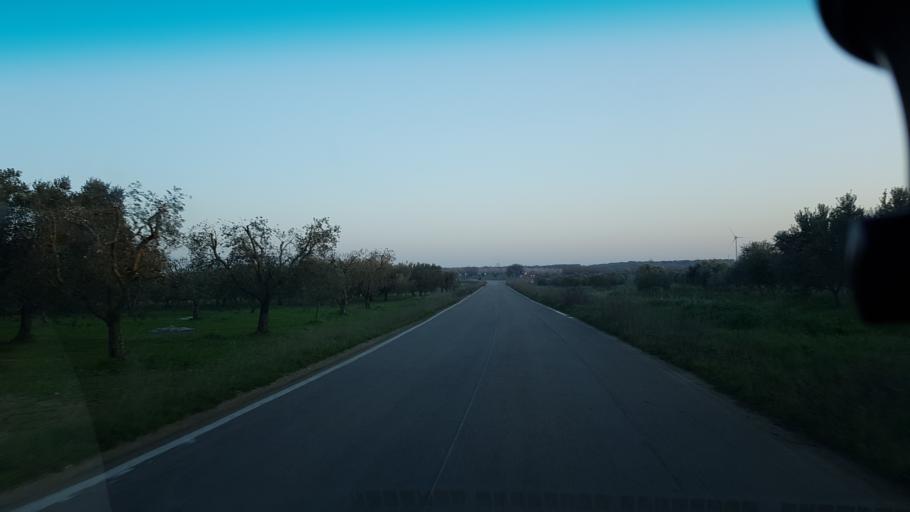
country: IT
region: Apulia
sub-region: Provincia di Brindisi
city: Mesagne
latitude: 40.6220
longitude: 17.7839
